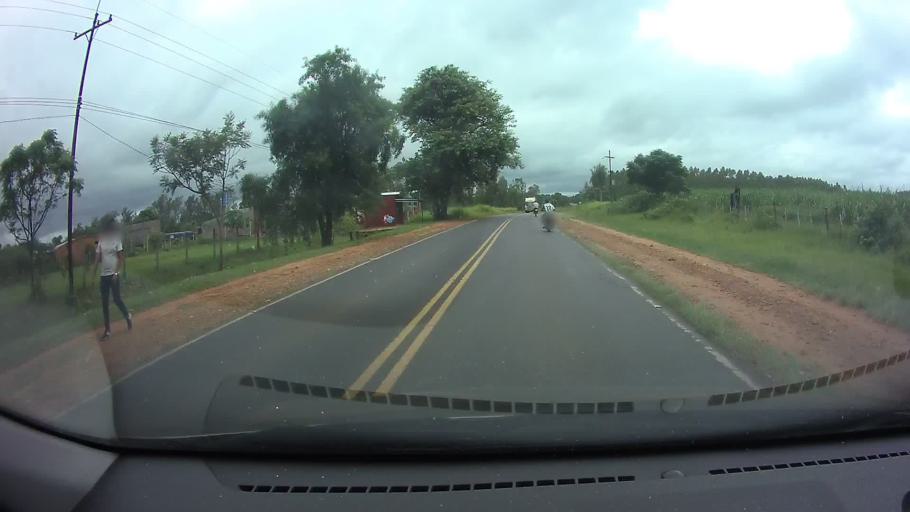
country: PY
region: Central
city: Guarambare
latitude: -25.5065
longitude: -57.4845
